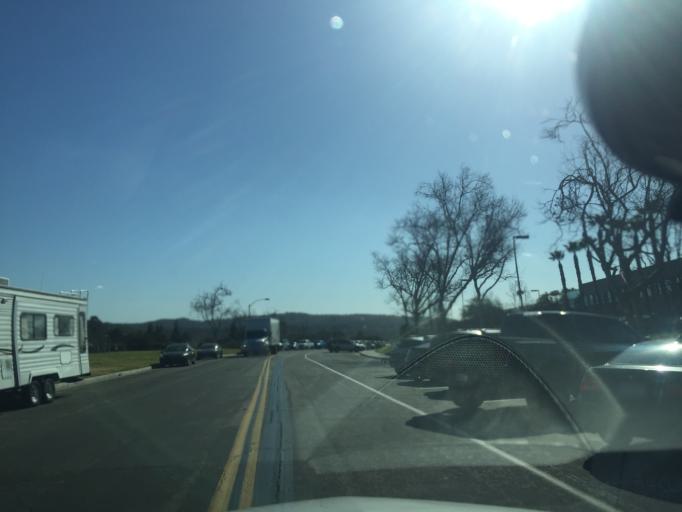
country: US
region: California
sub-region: San Diego County
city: Poway
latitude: 32.9606
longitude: -117.0948
